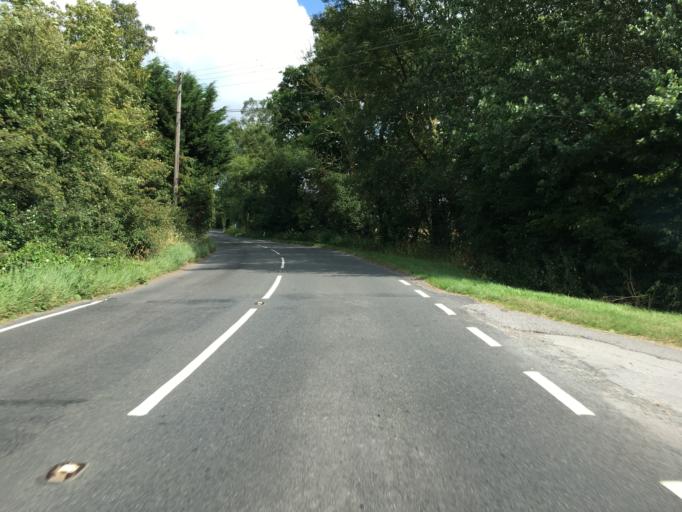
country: GB
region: England
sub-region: Kent
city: Tenterden
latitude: 51.0602
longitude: 0.7184
